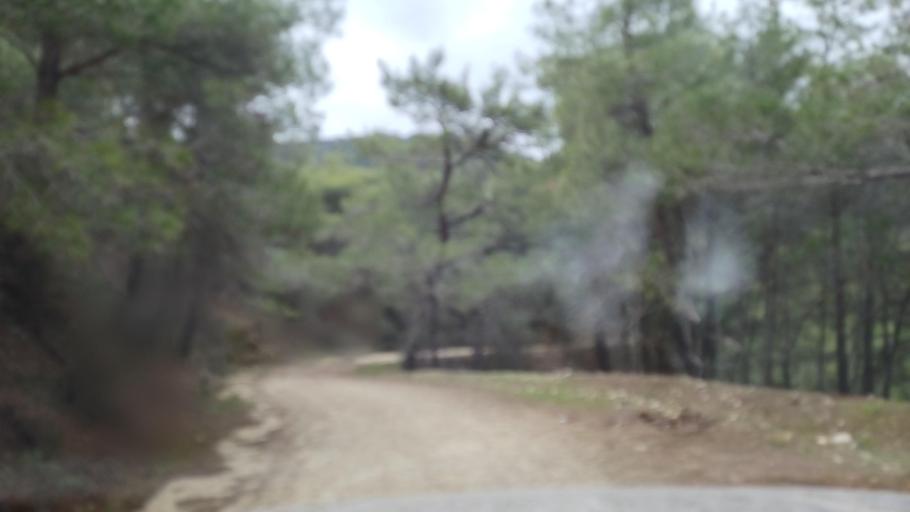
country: CY
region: Limassol
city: Pachna
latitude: 34.7734
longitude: 32.6941
